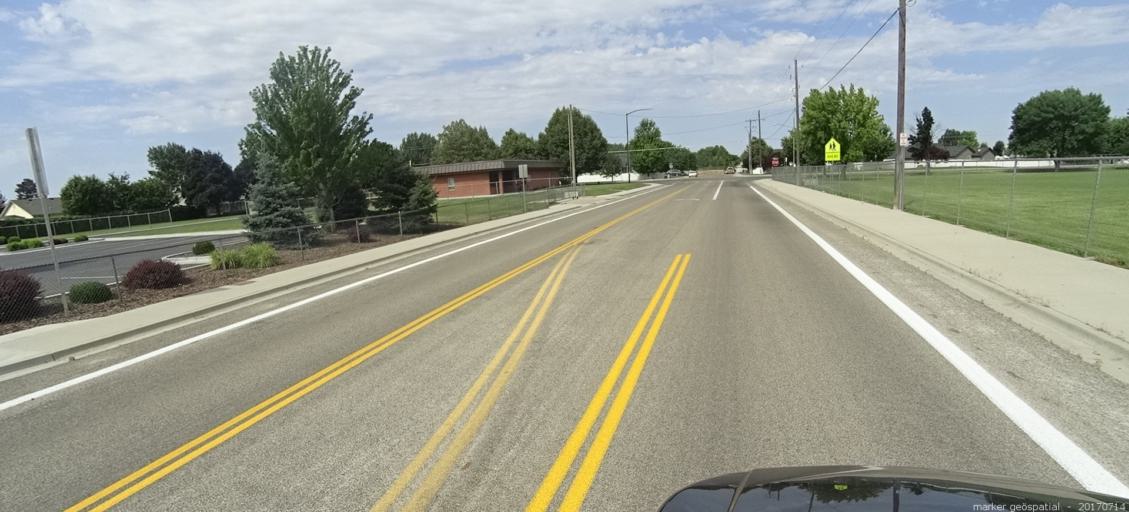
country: US
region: Idaho
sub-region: Ada County
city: Kuna
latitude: 43.4957
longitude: -116.4322
